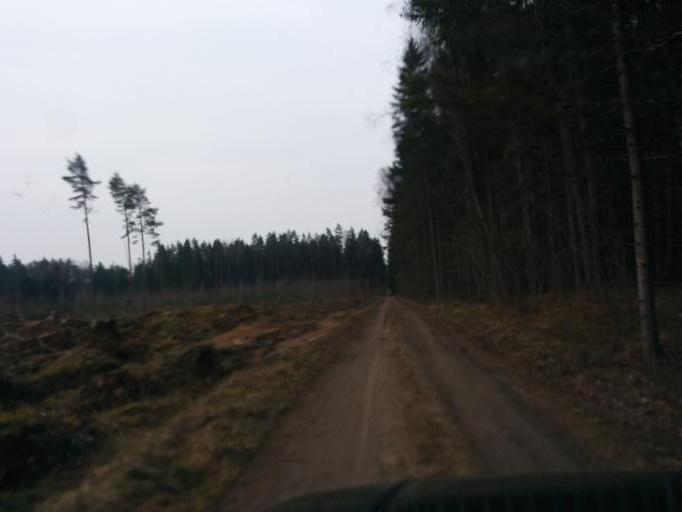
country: LV
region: Ikskile
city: Ikskile
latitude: 56.8087
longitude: 24.4818
